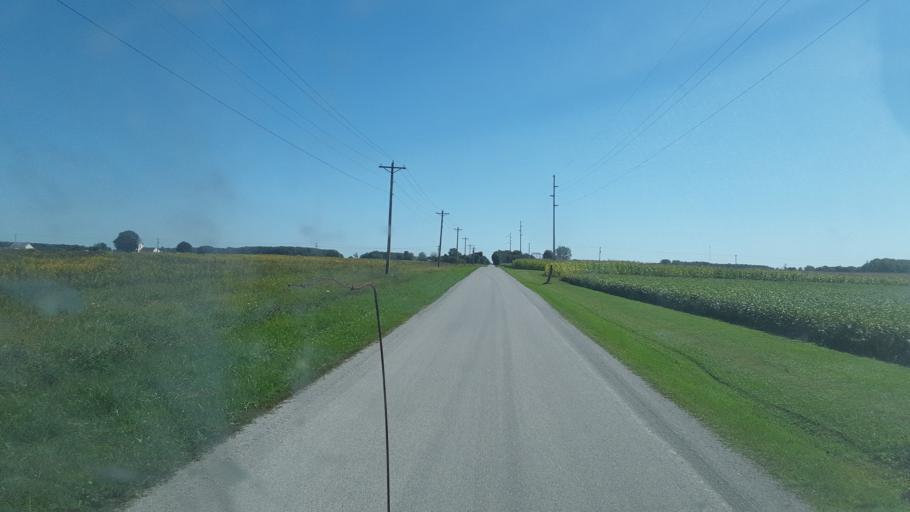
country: US
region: Ohio
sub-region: Seneca County
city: Tiffin
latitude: 40.9645
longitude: -83.1172
